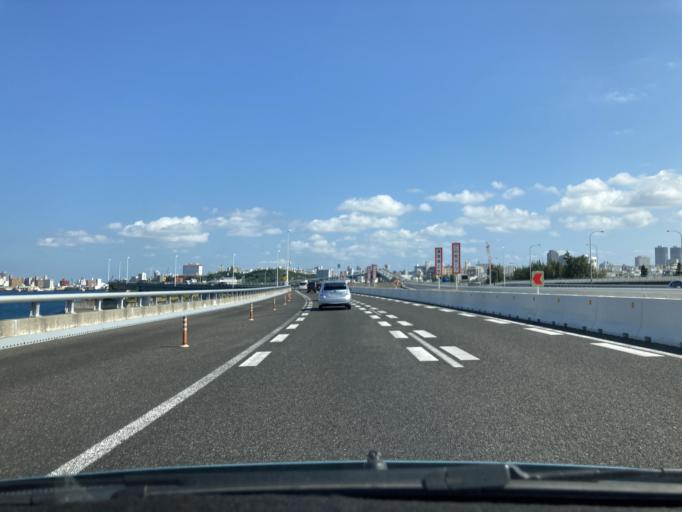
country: JP
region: Okinawa
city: Naha-shi
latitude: 26.2218
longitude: 127.6701
